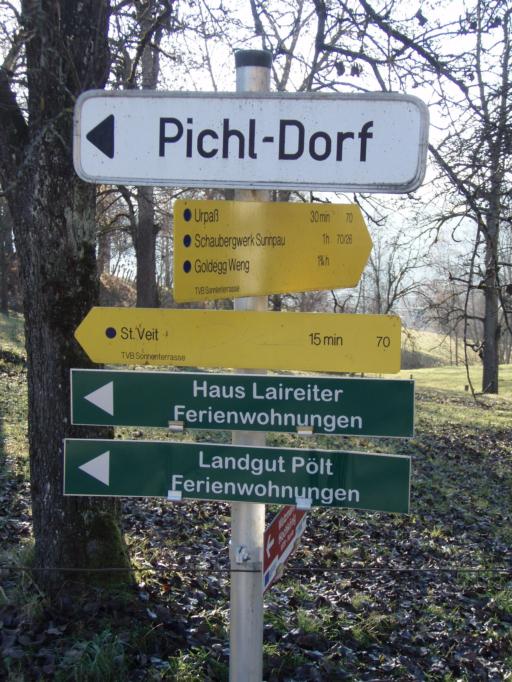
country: AT
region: Salzburg
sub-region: Politischer Bezirk Sankt Johann im Pongau
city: Sankt Veit im Pongau
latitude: 47.3330
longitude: 13.1434
